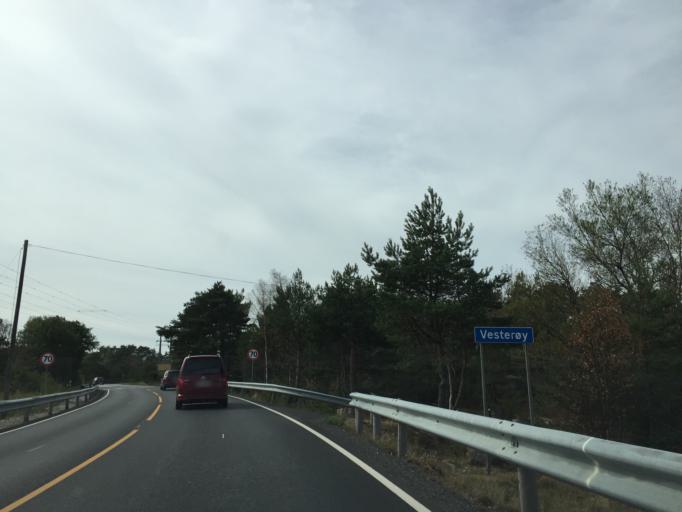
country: NO
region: Ostfold
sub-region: Fredrikstad
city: Fredrikstad
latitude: 59.1207
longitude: 10.9095
